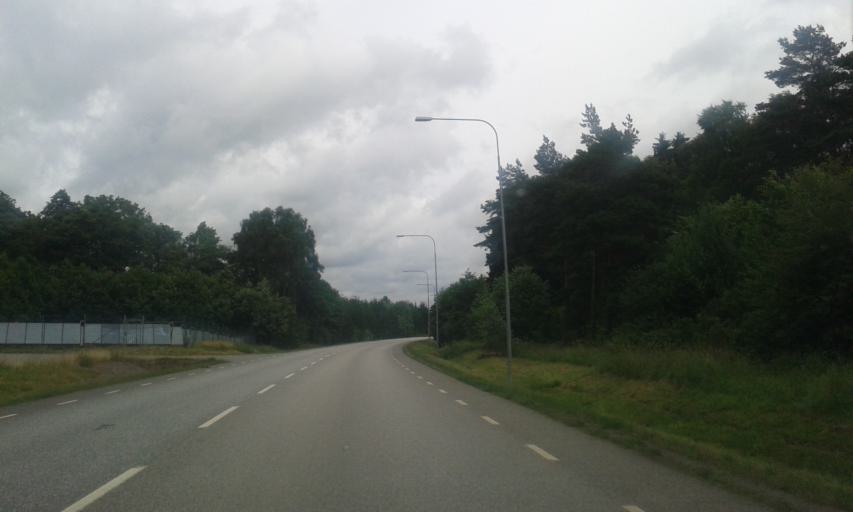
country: SE
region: Vaestra Goetaland
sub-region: Kungalvs Kommun
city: Kungalv
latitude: 57.8651
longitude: 11.8981
